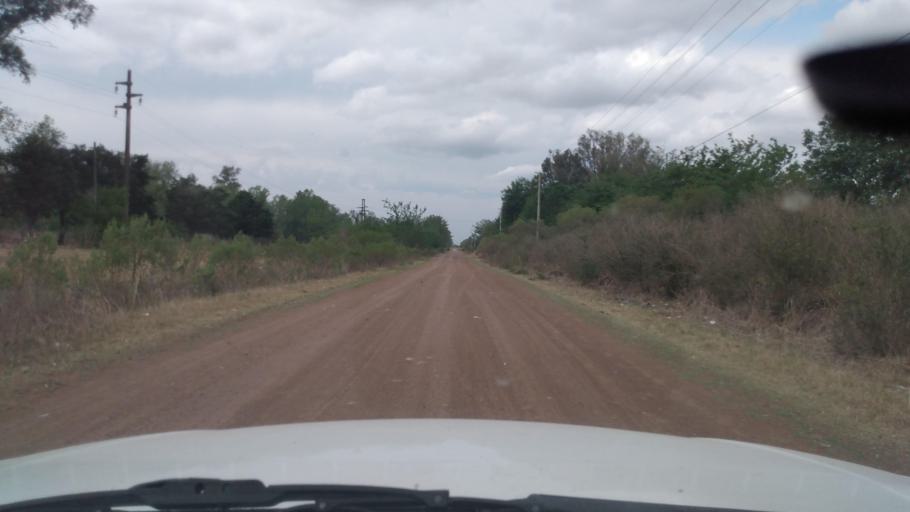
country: AR
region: Buenos Aires
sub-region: Partido de Lujan
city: Lujan
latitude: -34.5588
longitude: -59.1843
